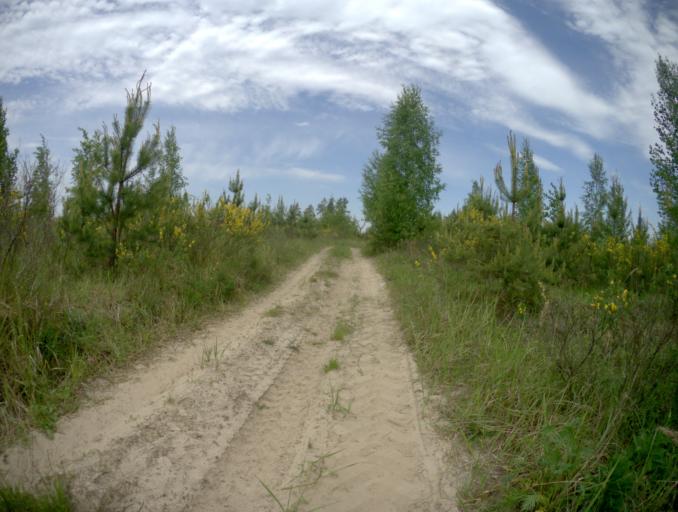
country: RU
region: Vladimir
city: Ivanishchi
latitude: 55.7070
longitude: 40.4687
